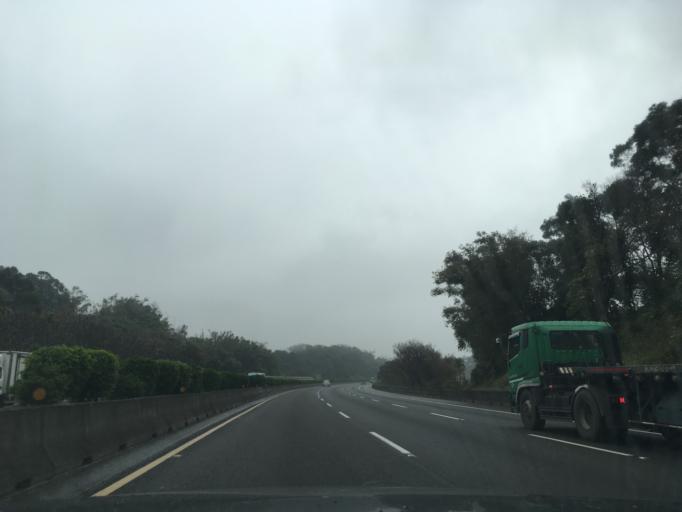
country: TW
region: Taiwan
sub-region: Hsinchu
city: Hsinchu
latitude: 24.7077
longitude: 120.9291
